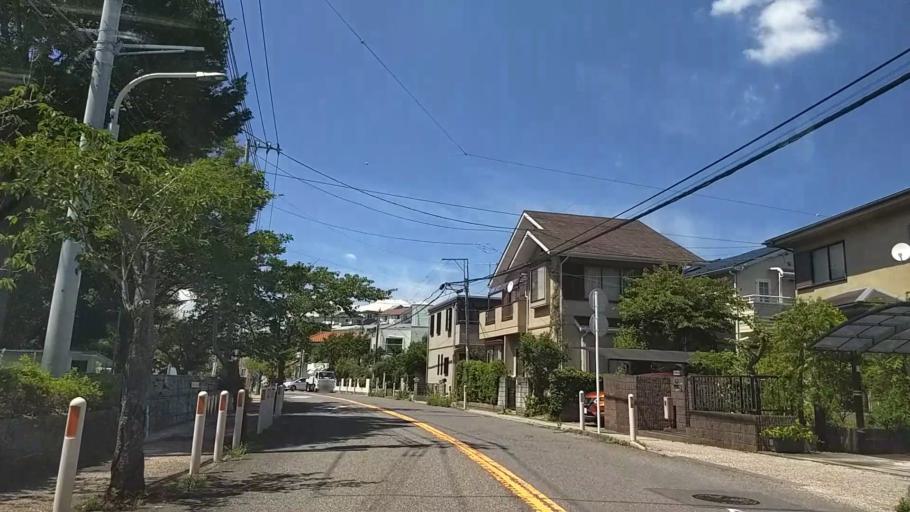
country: JP
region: Kanagawa
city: Zushi
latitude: 35.3008
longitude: 139.5937
